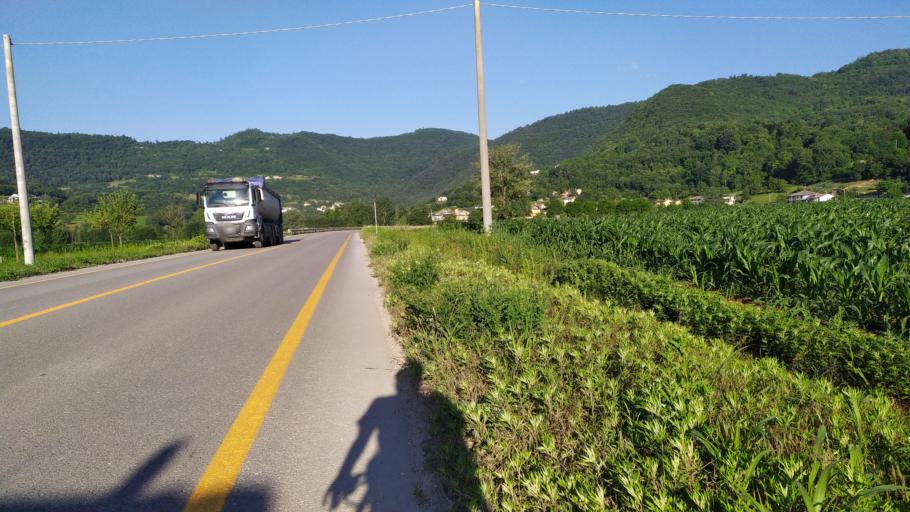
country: IT
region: Veneto
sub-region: Provincia di Vicenza
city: Isola Vicentina
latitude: 45.6311
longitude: 11.4246
